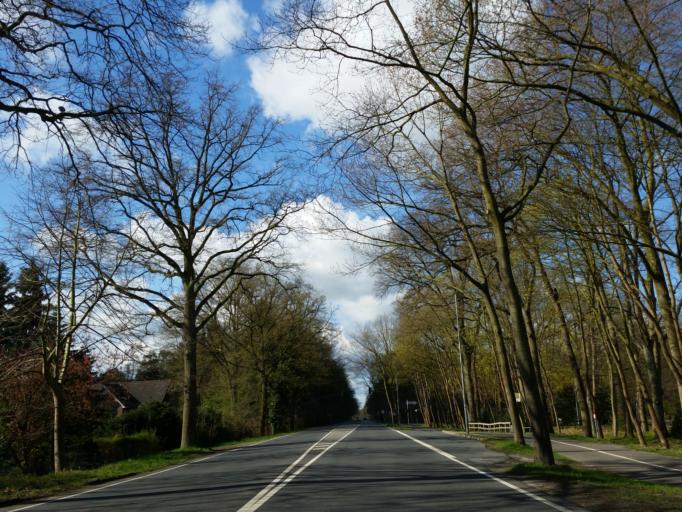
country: DE
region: Lower Saxony
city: Rotenburg
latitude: 53.0971
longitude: 9.3775
